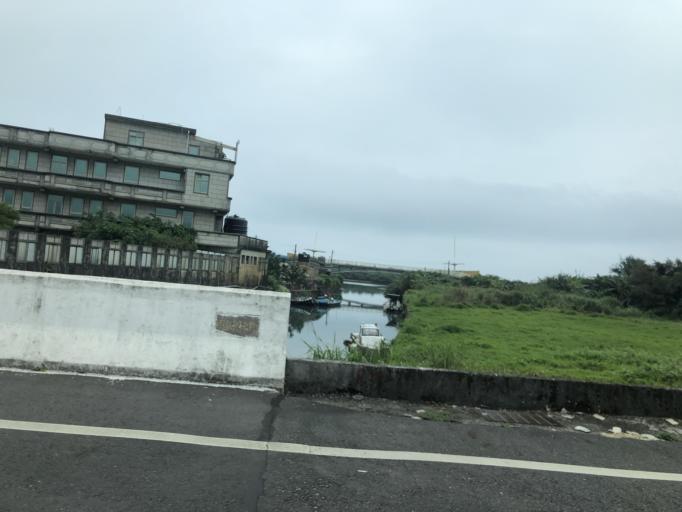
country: TW
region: Taiwan
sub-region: Keelung
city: Keelung
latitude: 25.2215
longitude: 121.6461
